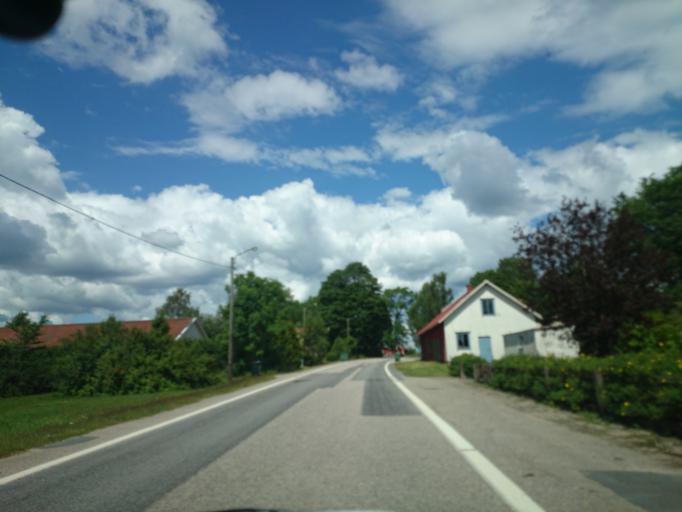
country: SE
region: Joenkoeping
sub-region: Varnamo Kommun
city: Forsheda
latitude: 57.0657
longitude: 13.8605
